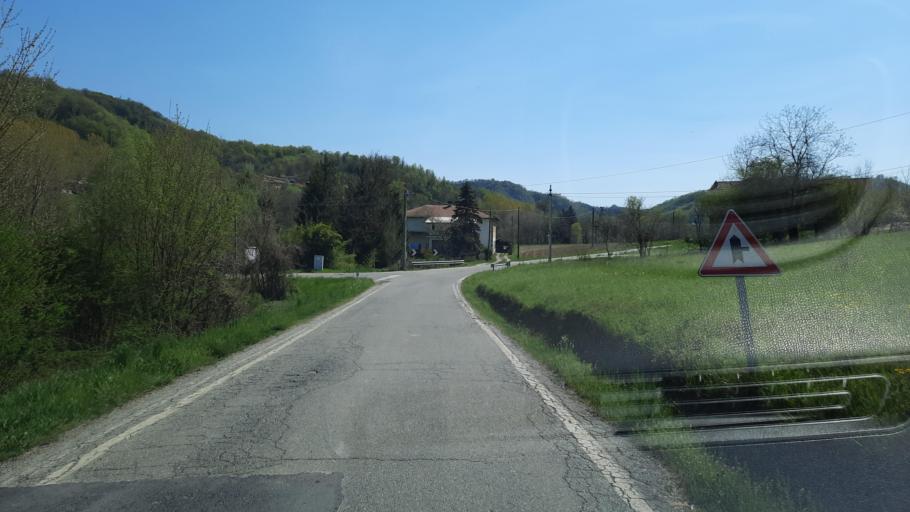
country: IT
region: Piedmont
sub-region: Provincia di Alessandria
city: Moncestino
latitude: 45.1465
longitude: 8.1281
